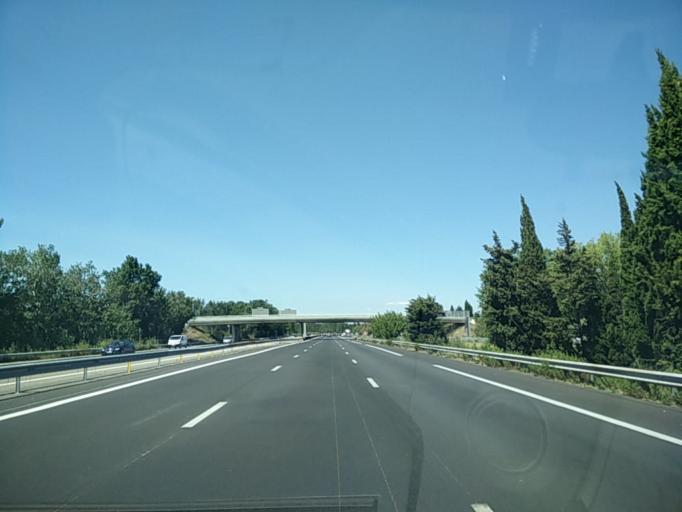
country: FR
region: Provence-Alpes-Cote d'Azur
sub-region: Departement du Vaucluse
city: Orange
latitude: 44.1336
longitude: 4.7864
